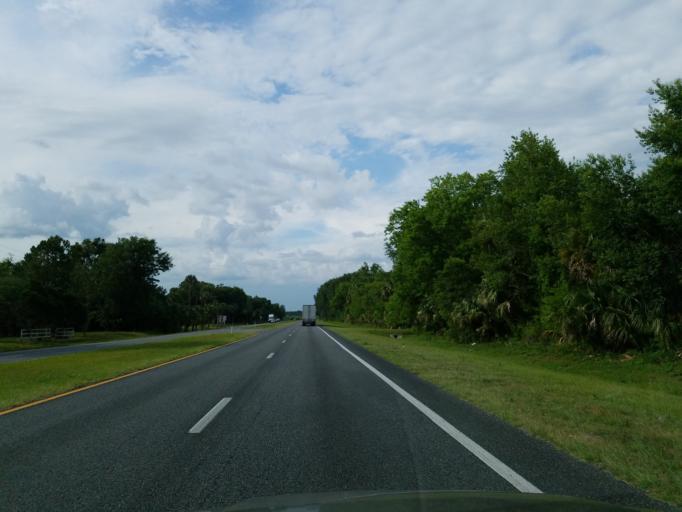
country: US
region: Florida
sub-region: Marion County
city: Citra
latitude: 29.4302
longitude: -82.1098
